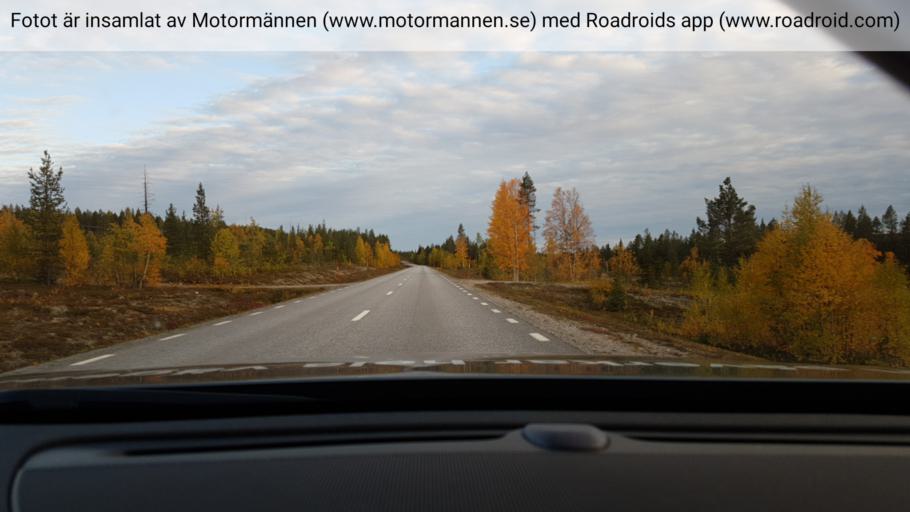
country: SE
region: Norrbotten
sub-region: Jokkmokks Kommun
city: Jokkmokk
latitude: 66.3847
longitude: 19.7121
